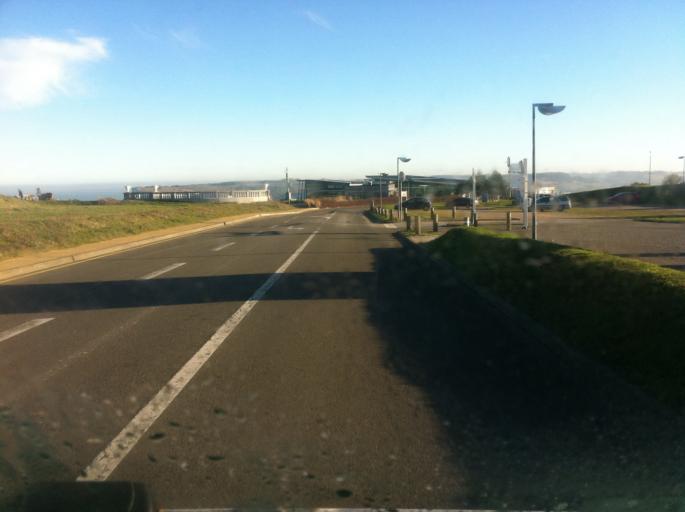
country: FR
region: Haute-Normandie
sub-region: Departement de la Seine-Maritime
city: Le Treport
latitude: 50.0588
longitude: 1.3650
